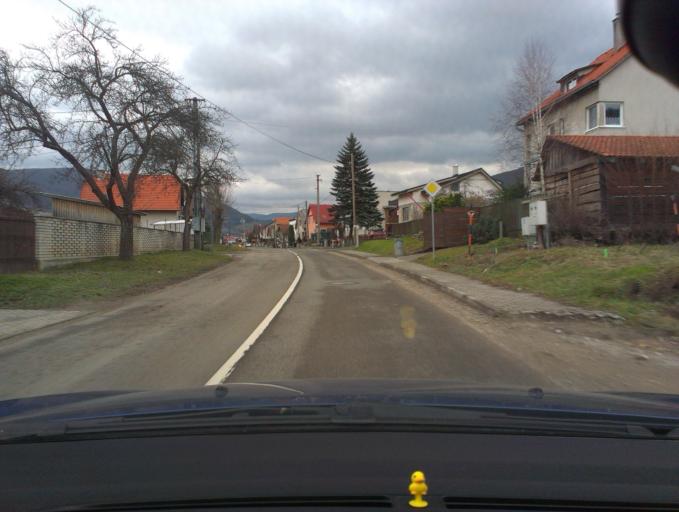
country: SK
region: Nitriansky
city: Trencianske Teplice
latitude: 48.8975
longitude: 18.2130
